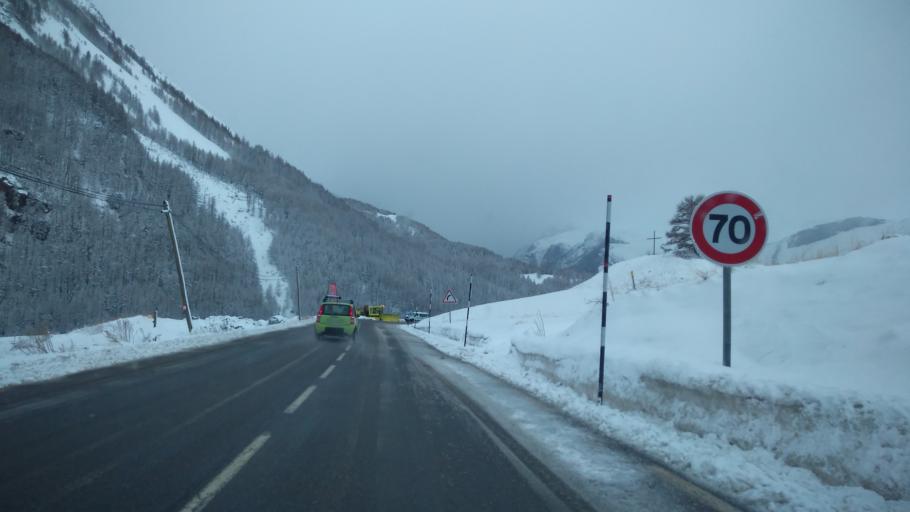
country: FR
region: Rhone-Alpes
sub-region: Departement de la Savoie
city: Valloire
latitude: 45.0415
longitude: 6.3428
